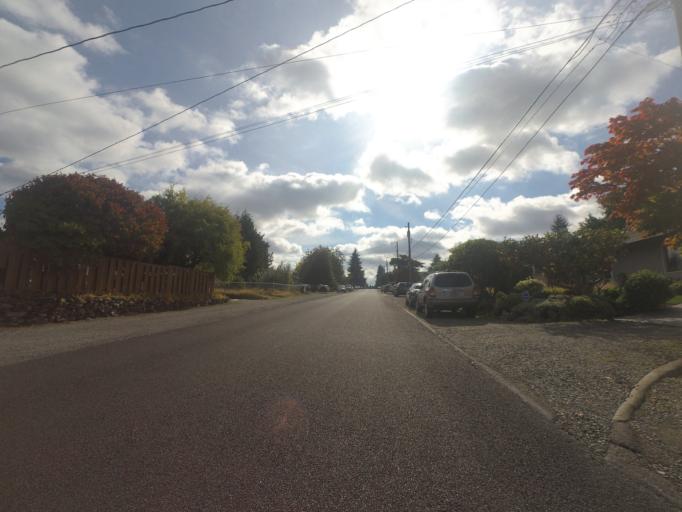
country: US
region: Washington
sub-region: Pierce County
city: University Place
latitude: 47.2345
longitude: -122.5441
